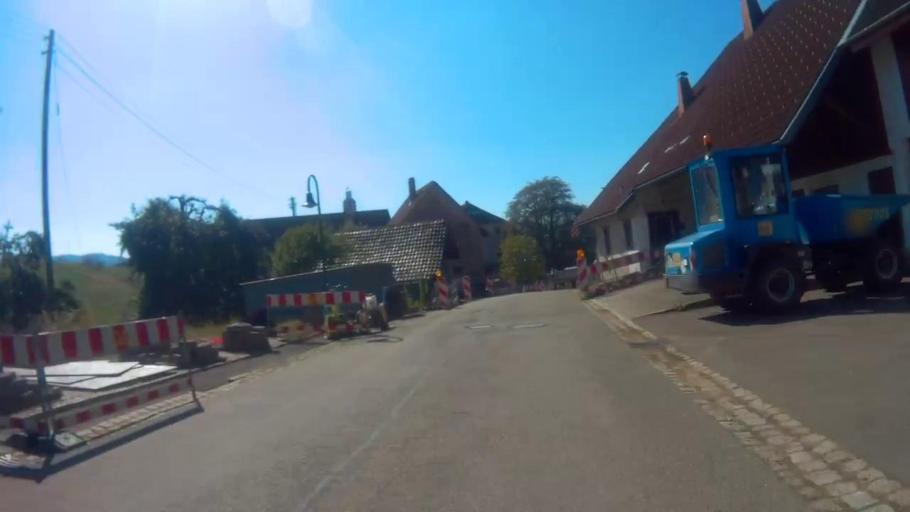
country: DE
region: Baden-Wuerttemberg
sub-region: Freiburg Region
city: Zell im Wiesental
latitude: 47.7167
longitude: 7.8376
